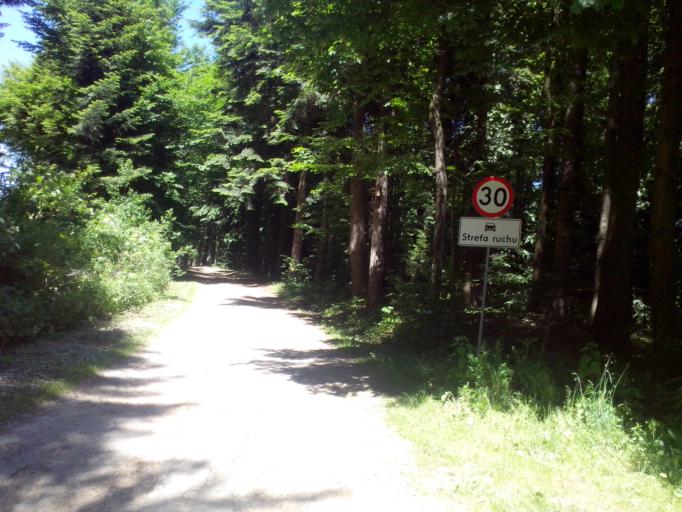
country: PL
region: Subcarpathian Voivodeship
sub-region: Powiat krosnienski
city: Leki
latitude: 49.8321
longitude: 21.6624
